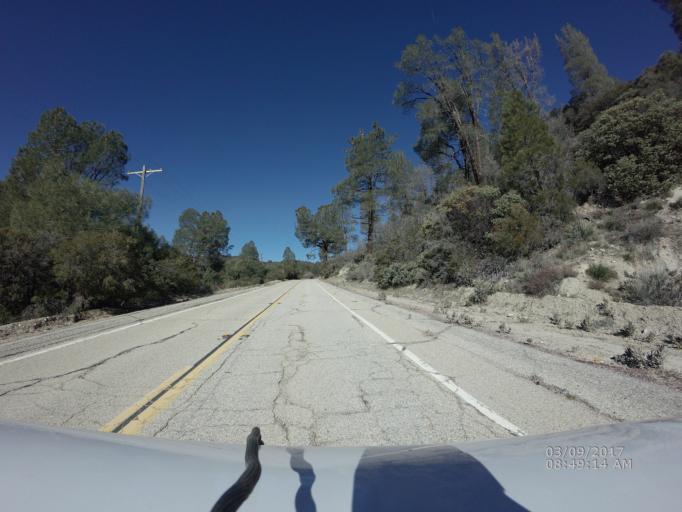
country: US
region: California
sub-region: Los Angeles County
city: Green Valley
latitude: 34.7024
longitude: -118.5254
